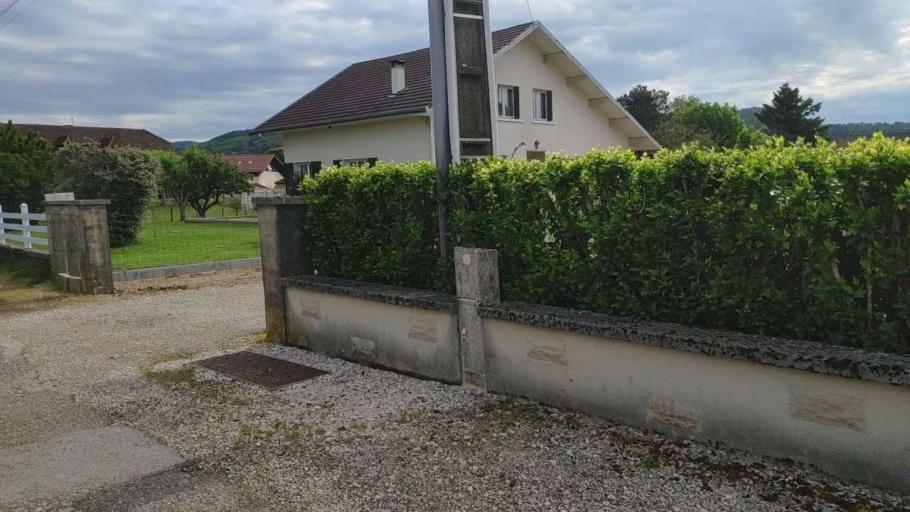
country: FR
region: Franche-Comte
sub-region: Departement du Jura
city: Perrigny
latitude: 46.7656
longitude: 5.5921
